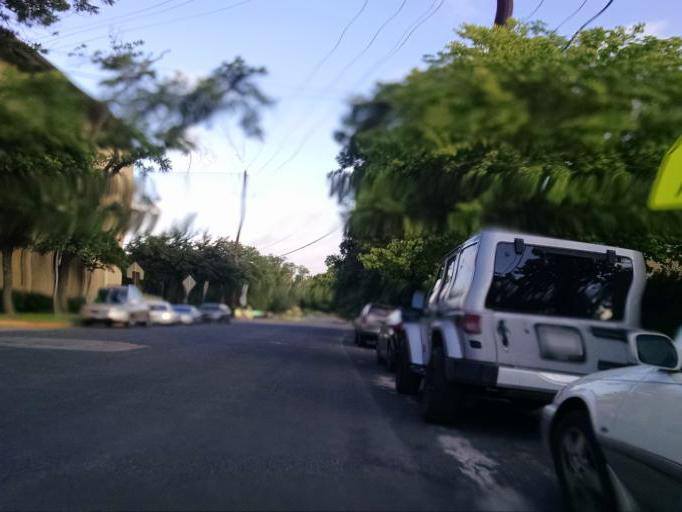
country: US
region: Texas
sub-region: Travis County
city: Austin
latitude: 30.3028
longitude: -97.7312
